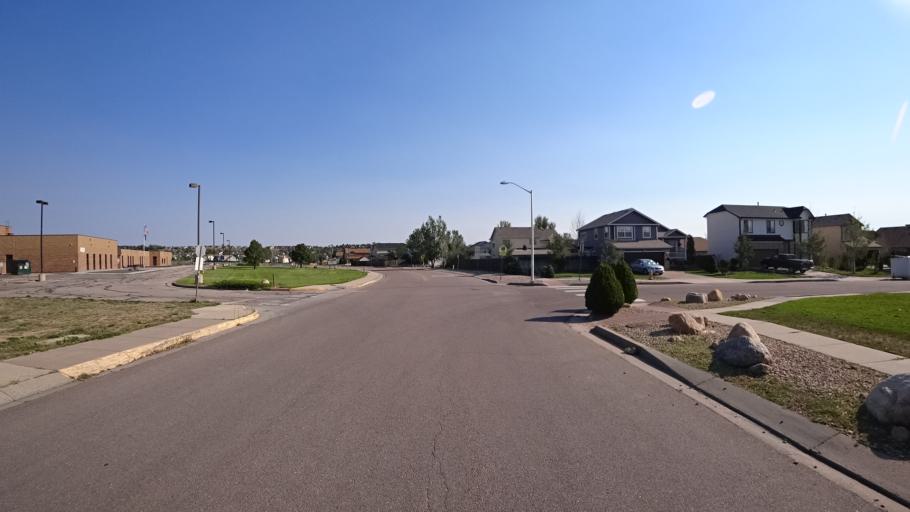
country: US
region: Colorado
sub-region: El Paso County
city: Stratmoor
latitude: 38.7695
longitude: -104.8056
